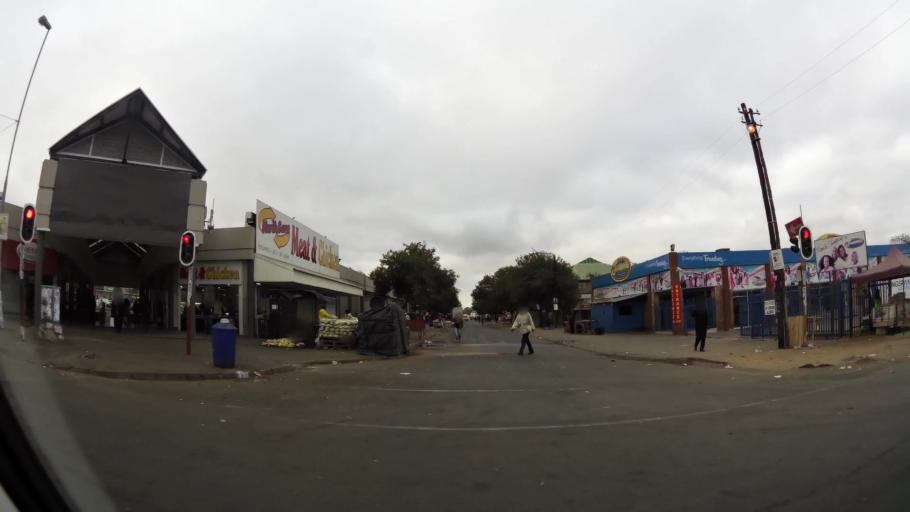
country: ZA
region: Limpopo
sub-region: Capricorn District Municipality
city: Polokwane
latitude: -23.9033
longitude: 29.4472
